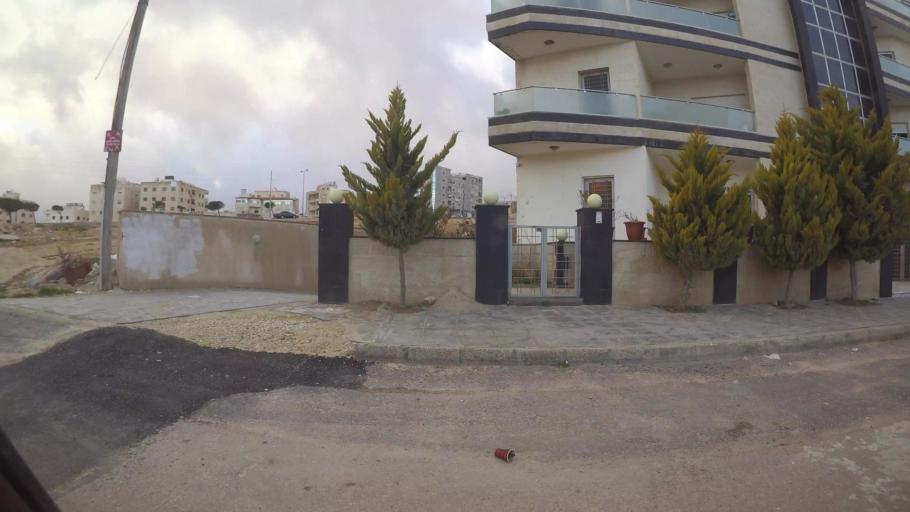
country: JO
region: Amman
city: Al Jubayhah
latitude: 32.0464
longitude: 35.8954
